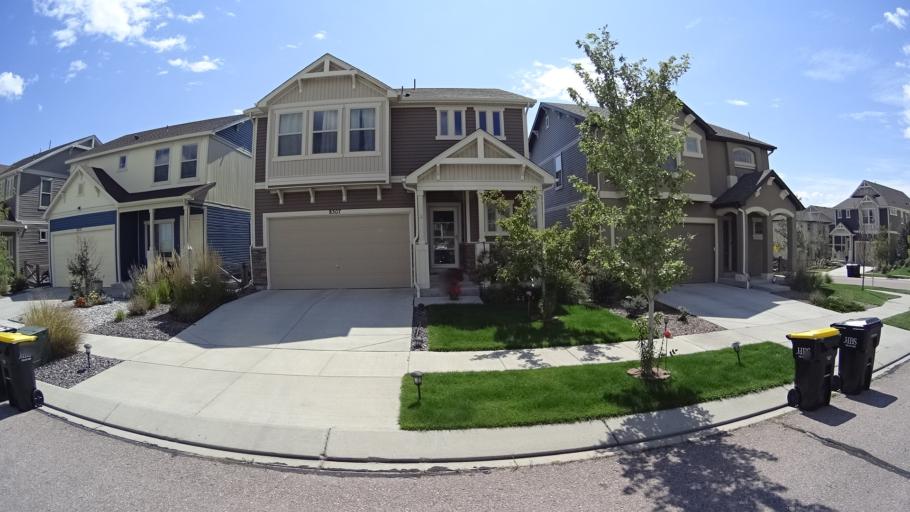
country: US
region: Colorado
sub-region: El Paso County
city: Cimarron Hills
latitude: 38.9278
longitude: -104.6735
